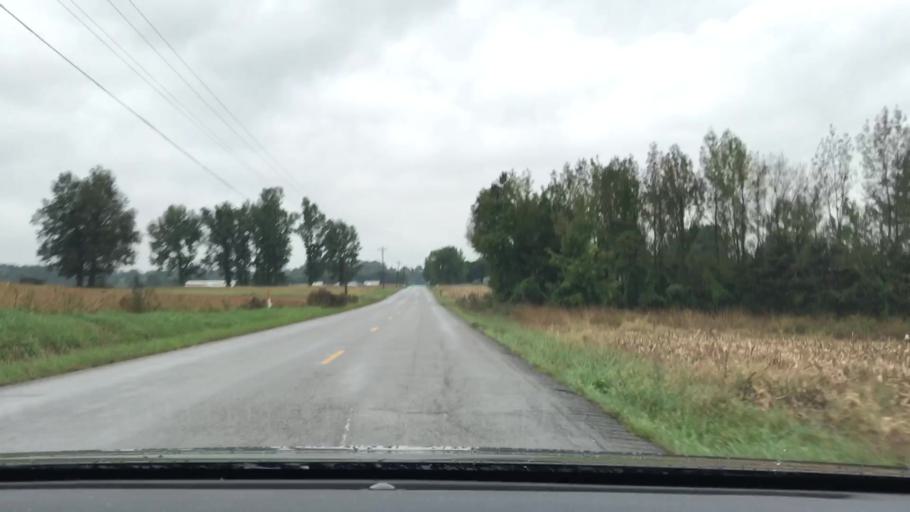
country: US
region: Kentucky
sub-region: McLean County
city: Calhoun
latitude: 37.4291
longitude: -87.2539
